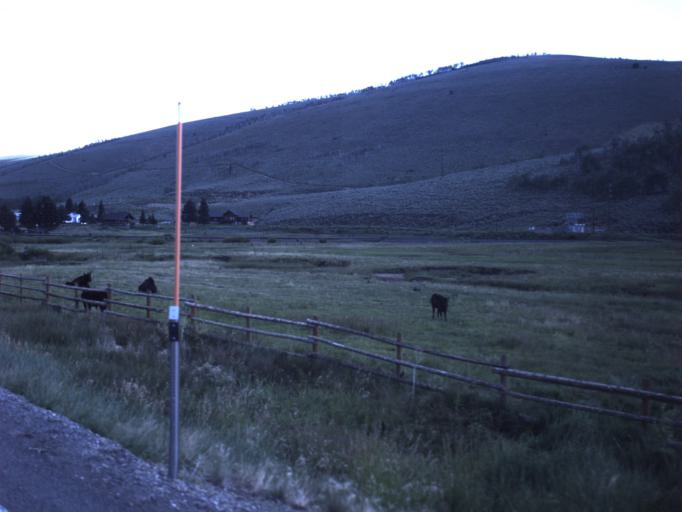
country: US
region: Utah
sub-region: Sanpete County
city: Fairview
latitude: 39.7205
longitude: -111.1625
